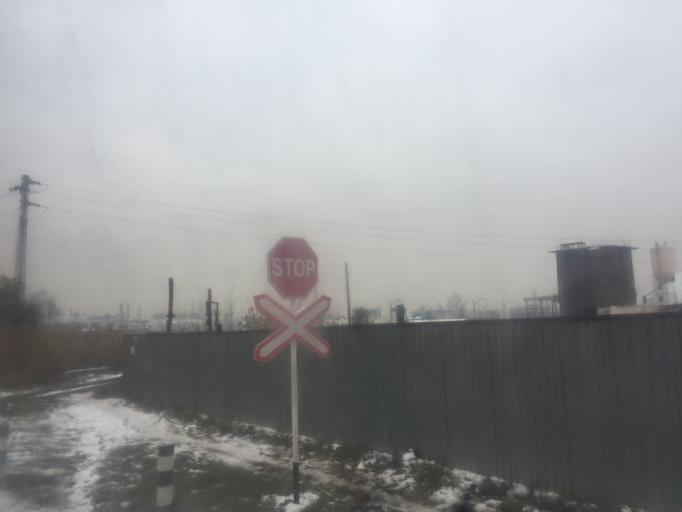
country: KZ
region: Astana Qalasy
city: Astana
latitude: 51.1995
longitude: 71.4106
